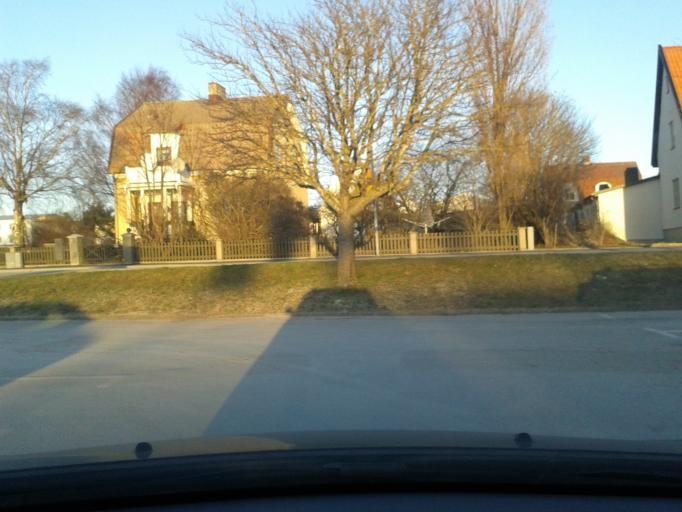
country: SE
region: Gotland
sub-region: Gotland
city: Visby
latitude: 57.6389
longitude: 18.3023
